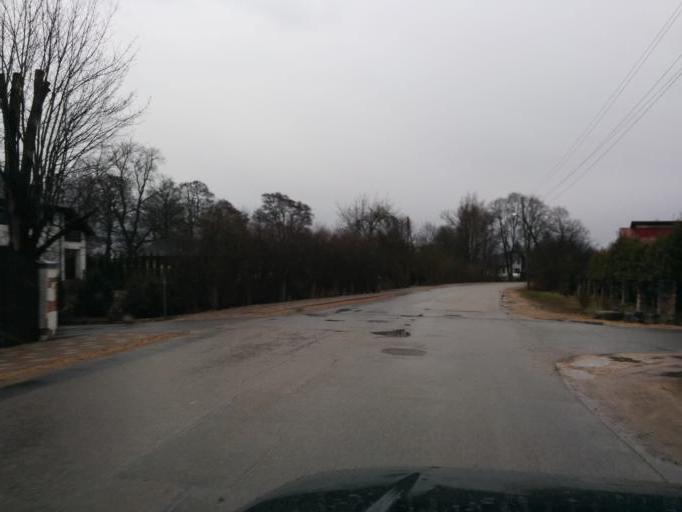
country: LV
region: Kekava
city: Kekava
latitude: 56.8733
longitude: 24.1841
